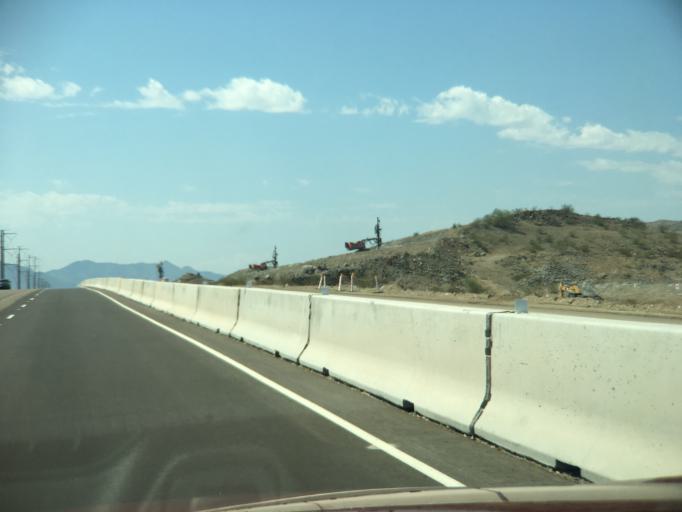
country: US
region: Arizona
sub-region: Maricopa County
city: Laveen
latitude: 33.2911
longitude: -112.0727
